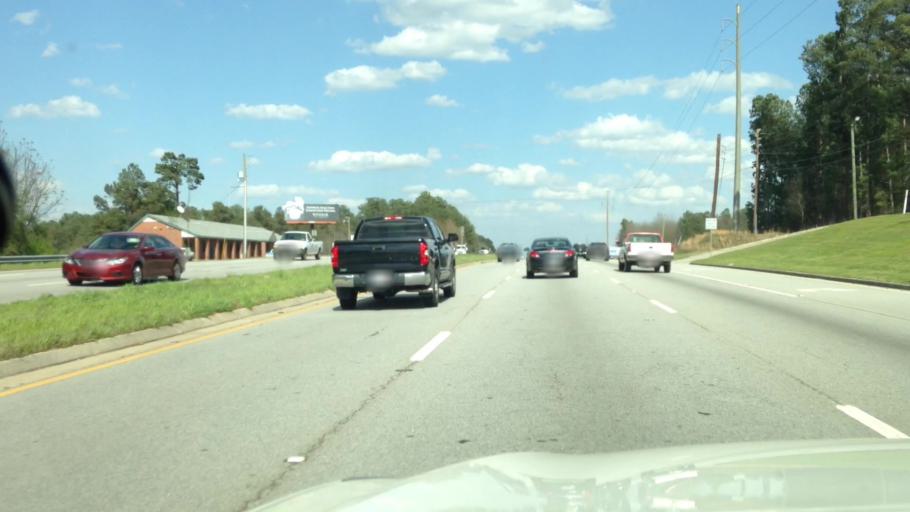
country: US
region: Georgia
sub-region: Columbia County
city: Martinez
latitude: 33.4449
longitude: -82.0934
